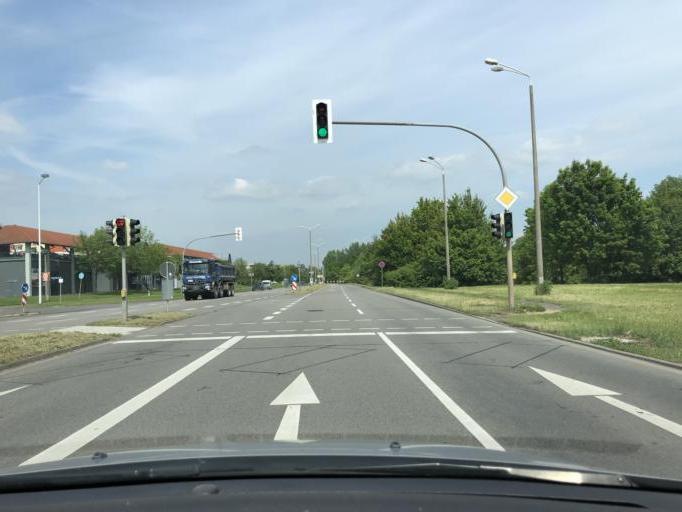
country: DE
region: Thuringia
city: Altenburg
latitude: 50.9957
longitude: 12.4236
